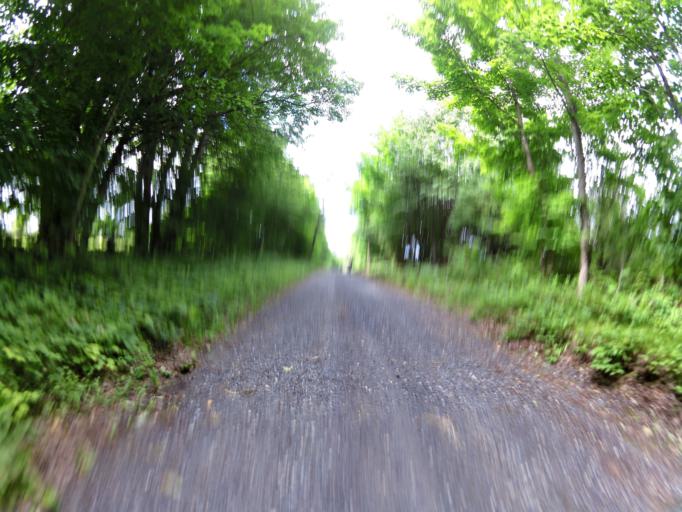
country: CA
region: Ontario
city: Perth
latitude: 45.0250
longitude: -76.5500
